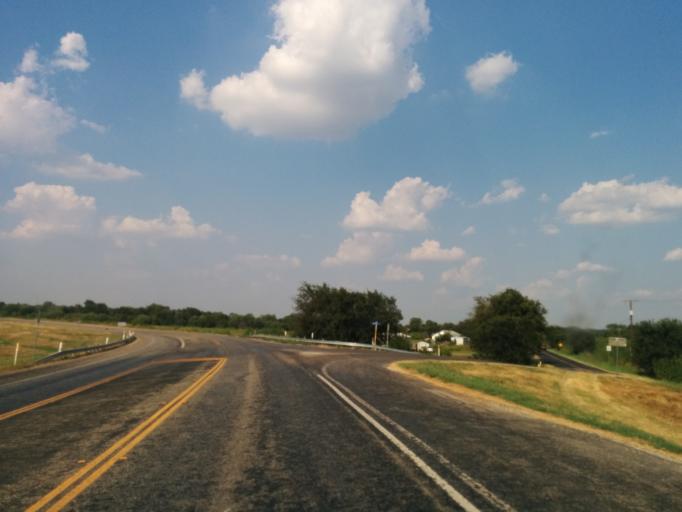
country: US
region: Texas
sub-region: Bexar County
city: Elmendorf
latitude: 29.3041
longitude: -98.2619
